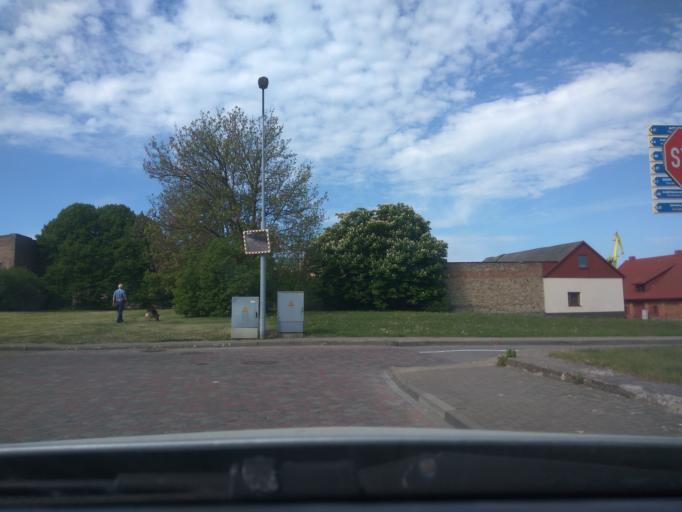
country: LV
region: Ventspils
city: Ventspils
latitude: 57.3975
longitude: 21.5653
